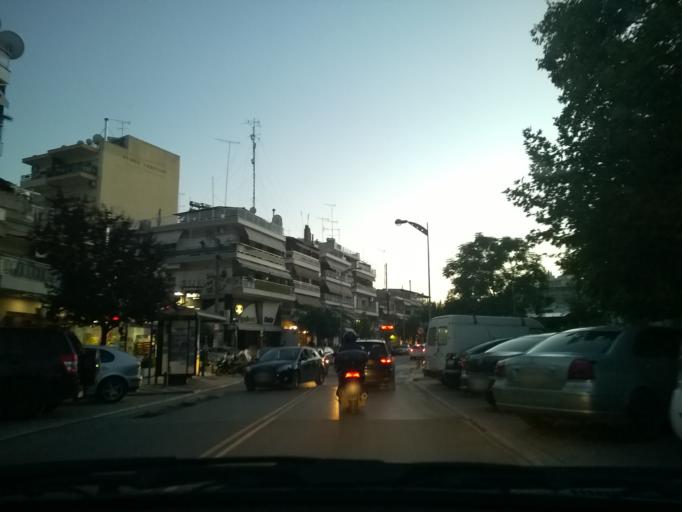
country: GR
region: Central Macedonia
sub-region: Nomos Thessalonikis
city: Polichni
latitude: 40.6595
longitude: 22.9442
